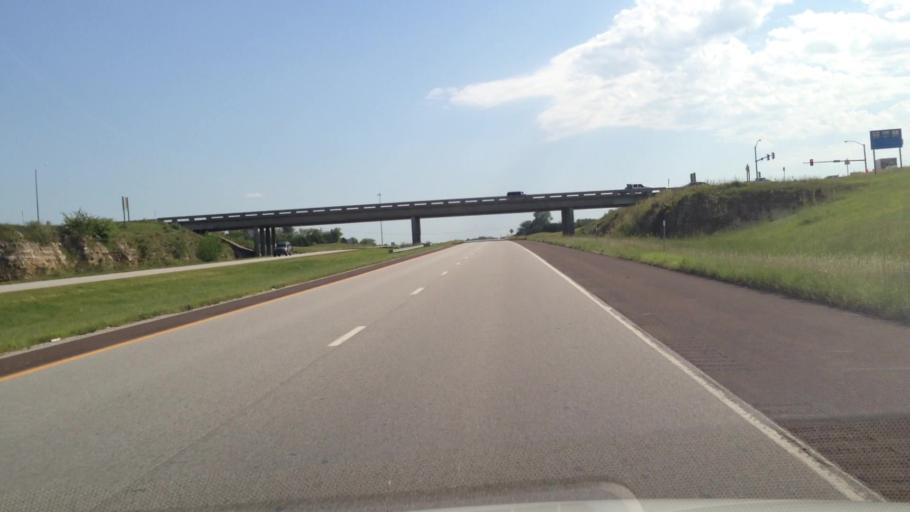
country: US
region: Kansas
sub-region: Miami County
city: Louisburg
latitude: 38.6224
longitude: -94.6952
